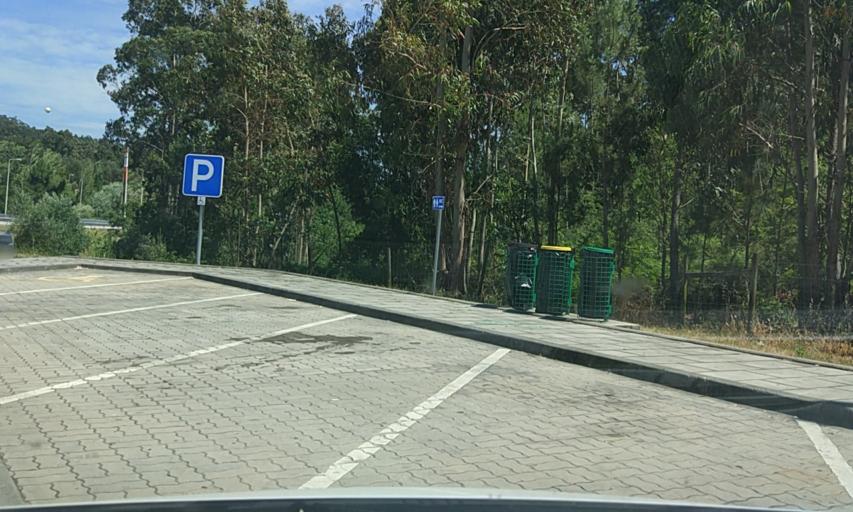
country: PT
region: Aveiro
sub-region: Mealhada
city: Pampilhosa do Botao
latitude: 40.2705
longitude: -8.4721
